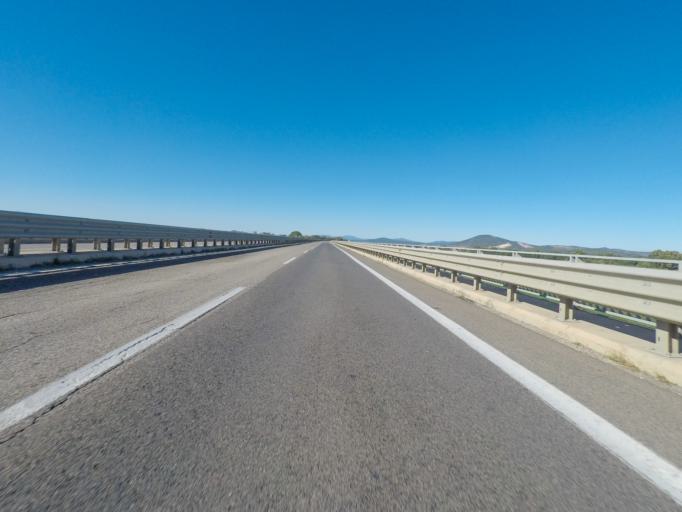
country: IT
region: Tuscany
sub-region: Provincia di Grosseto
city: Grosseto
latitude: 42.7541
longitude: 11.1433
